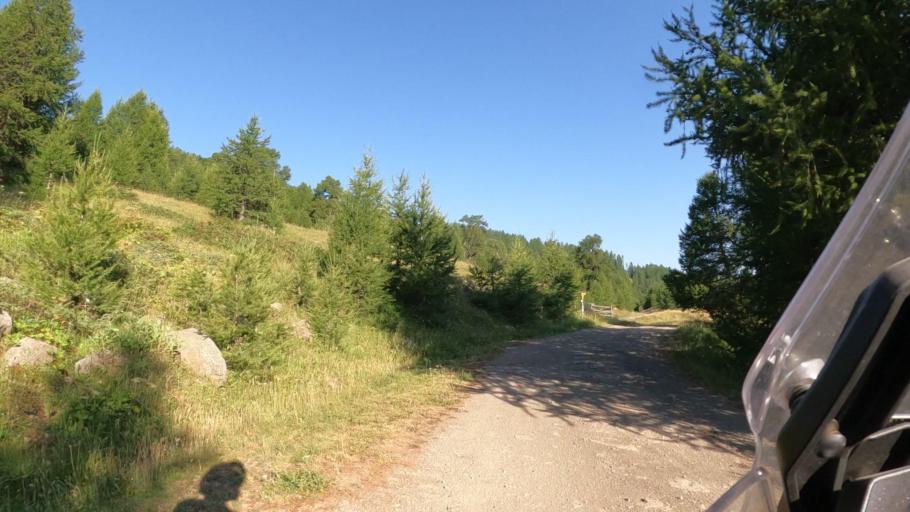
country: FR
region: Provence-Alpes-Cote d'Azur
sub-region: Departement des Hautes-Alpes
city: Guillestre
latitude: 44.6113
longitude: 6.6493
